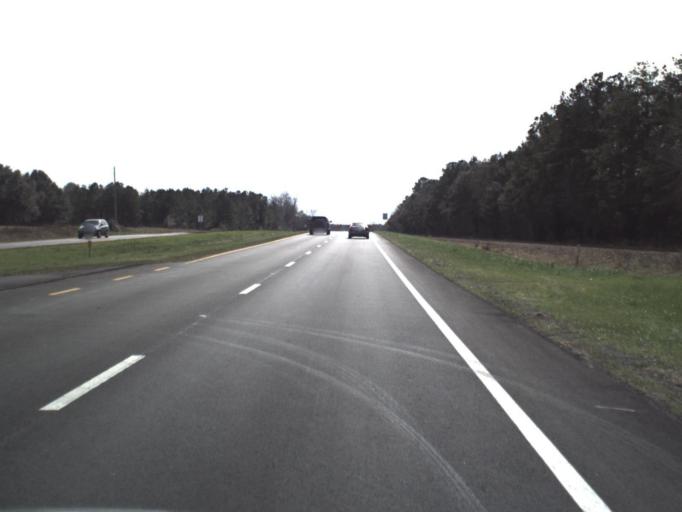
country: US
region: Florida
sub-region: Washington County
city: Chipley
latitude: 30.6863
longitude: -85.3933
